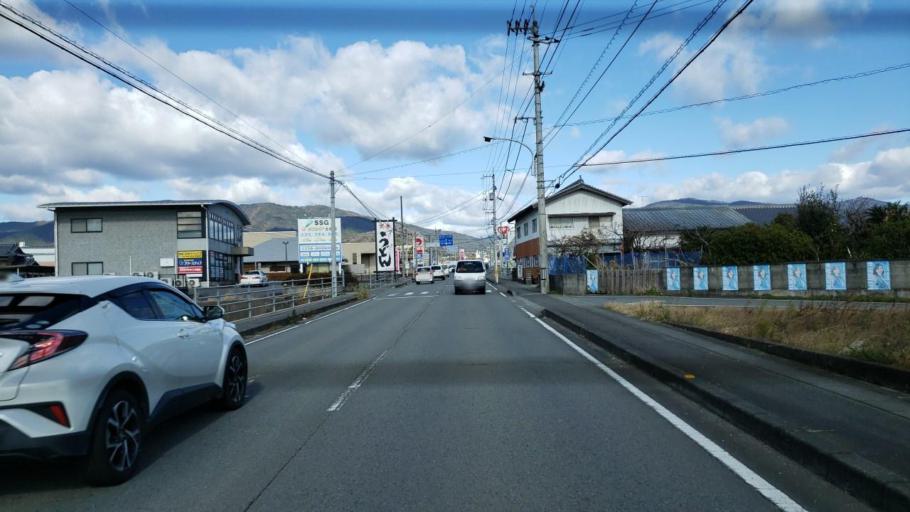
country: JP
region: Tokushima
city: Kamojimacho-jogejima
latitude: 34.0996
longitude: 134.3451
